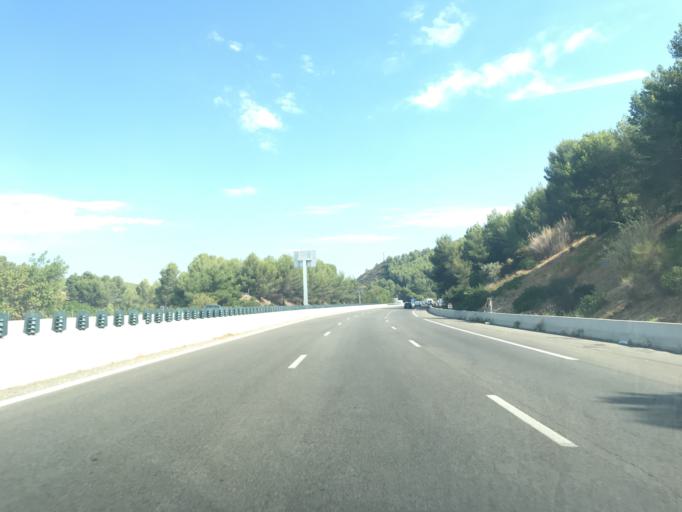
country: FR
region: Provence-Alpes-Cote d'Azur
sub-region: Departement du Var
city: Bandol
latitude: 43.1552
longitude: 5.7655
